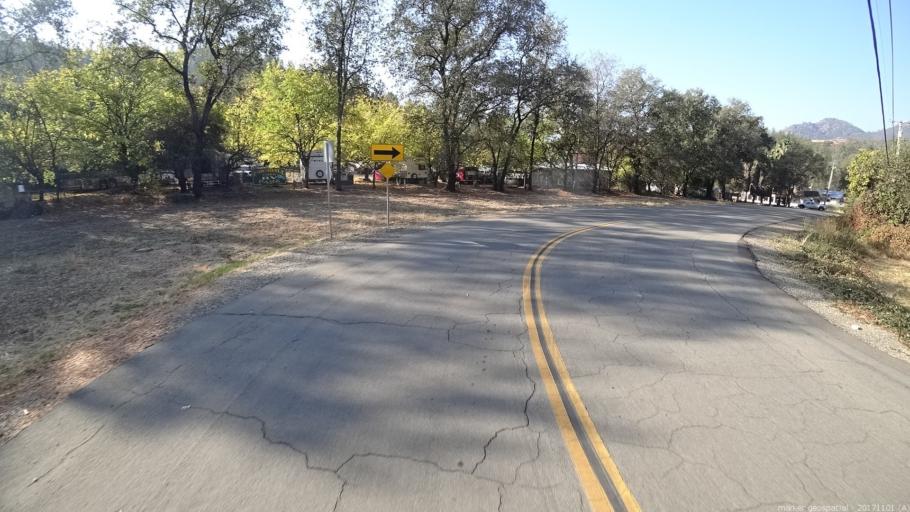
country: US
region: California
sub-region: Shasta County
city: Shasta Lake
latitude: 40.7247
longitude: -122.3220
